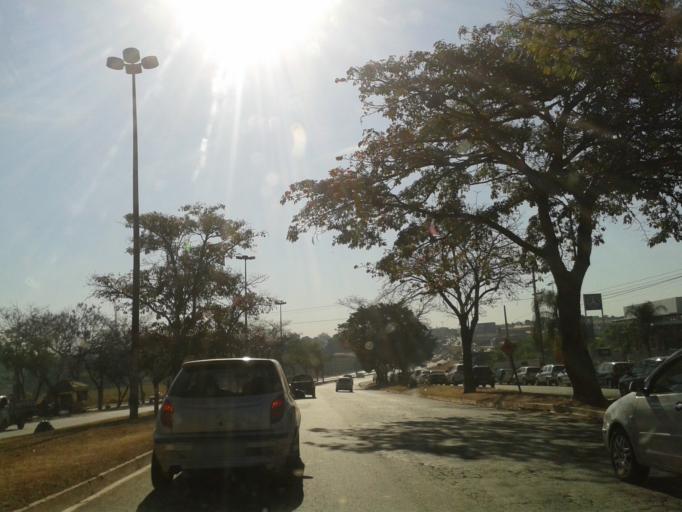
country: BR
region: Goias
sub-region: Goiania
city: Goiania
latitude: -16.6940
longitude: -49.3229
